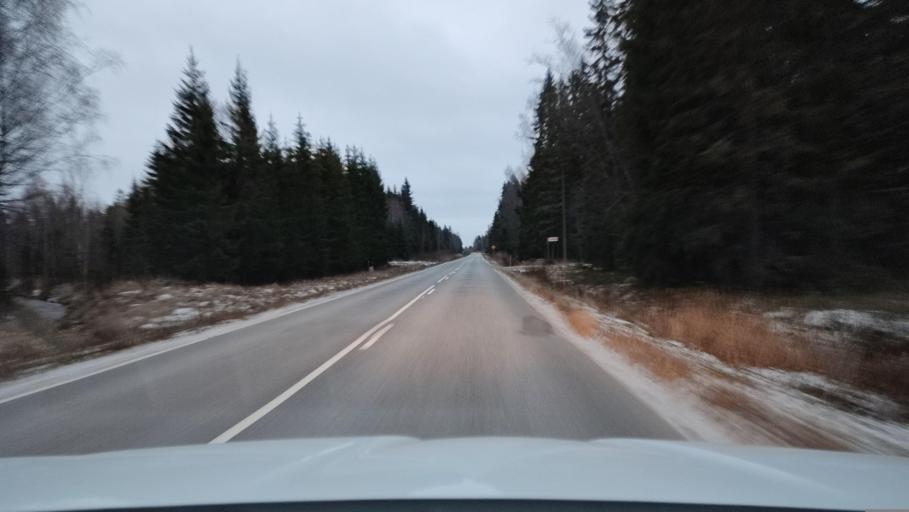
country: FI
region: Ostrobothnia
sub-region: Vaasa
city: Replot
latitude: 63.2382
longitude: 21.3897
